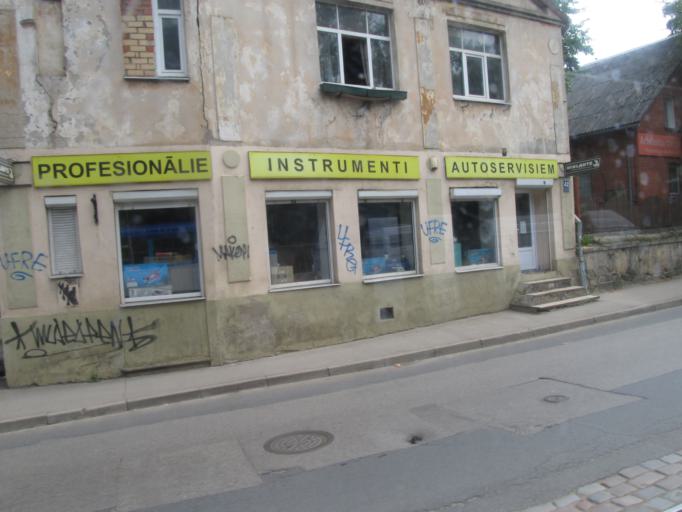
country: LV
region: Riga
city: Riga
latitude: 56.9514
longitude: 24.0639
